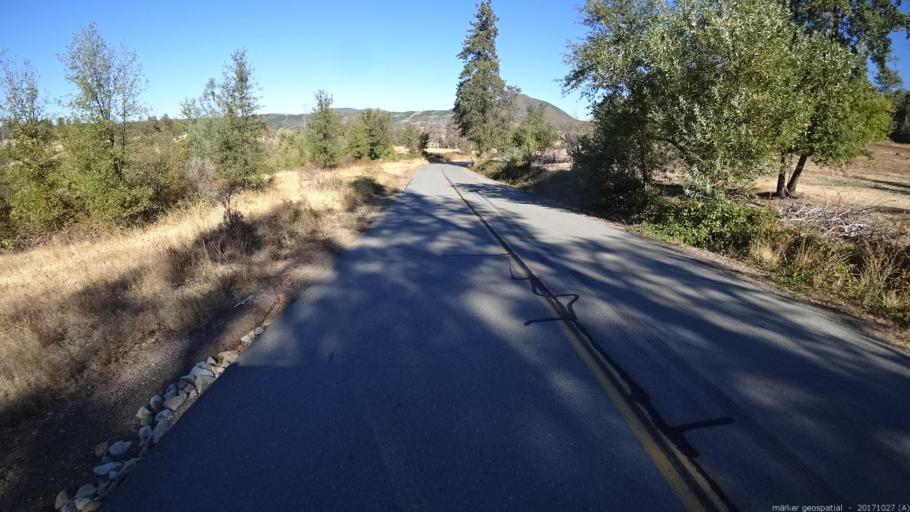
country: US
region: California
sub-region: Shasta County
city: Shingletown
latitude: 40.7658
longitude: -121.9699
